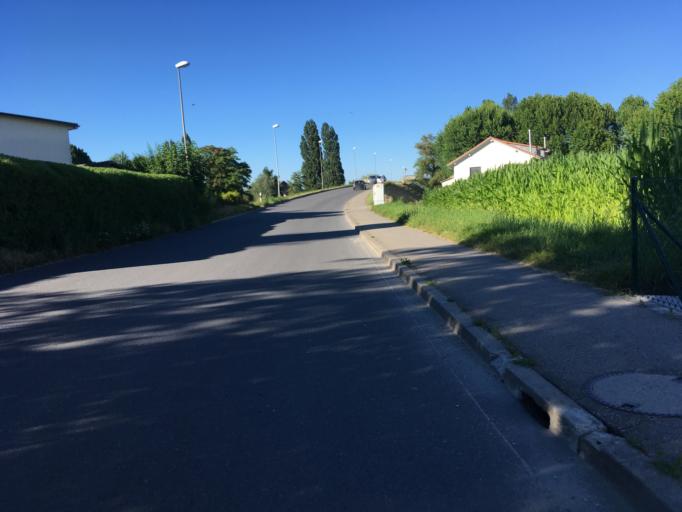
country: CH
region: Fribourg
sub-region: See District
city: Bas-Vully
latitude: 46.9625
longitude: 7.1136
